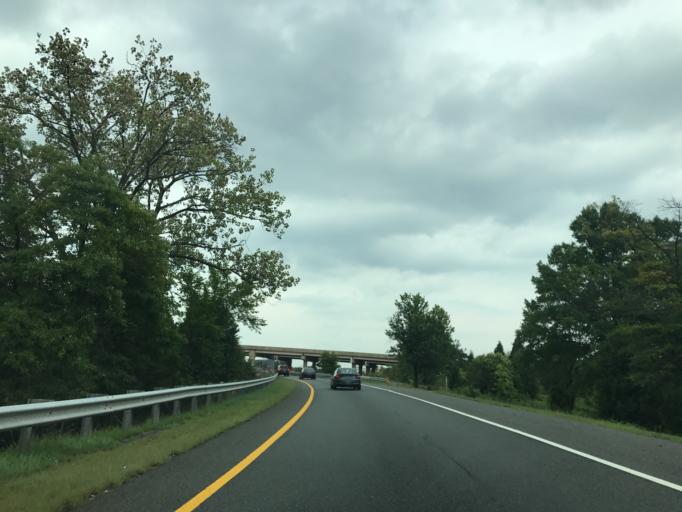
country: US
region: Maryland
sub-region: Baltimore County
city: Woodlawn
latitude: 39.3040
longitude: -76.7425
